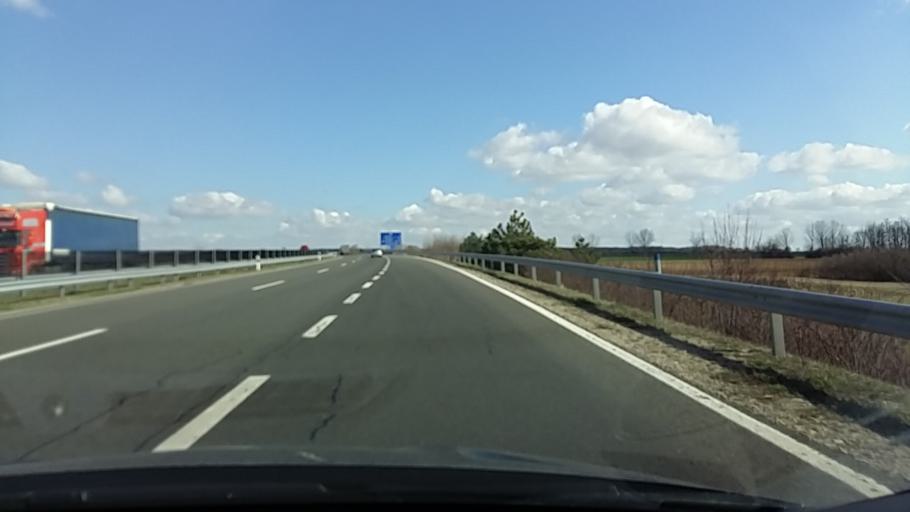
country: HU
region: Baranya
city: Kozarmisleny
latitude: 46.0187
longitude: 18.2935
